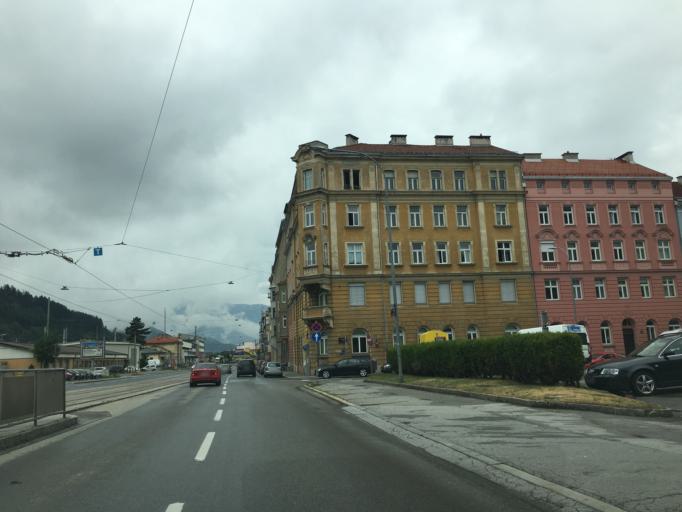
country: AT
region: Tyrol
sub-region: Innsbruck Stadt
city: Innsbruck
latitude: 47.2563
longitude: 11.3953
